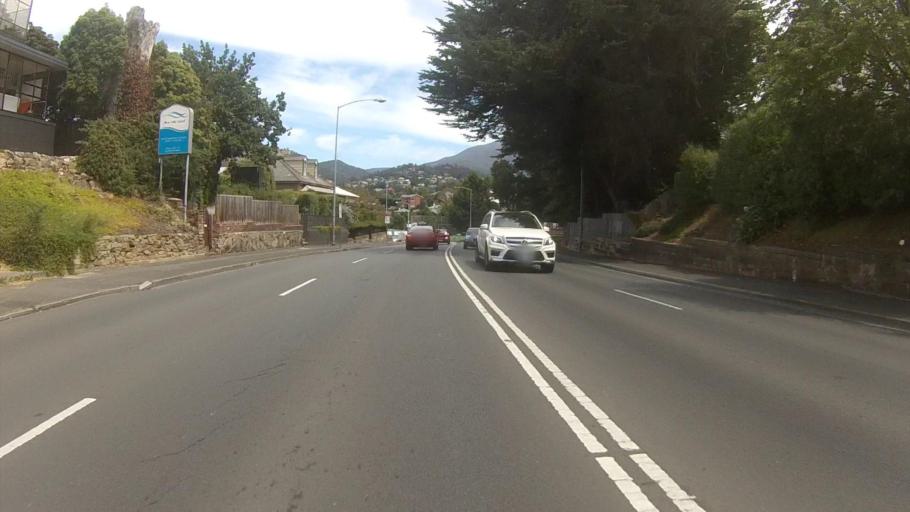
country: AU
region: Tasmania
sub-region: Hobart
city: Sandy Bay
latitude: -42.8913
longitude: 147.3278
